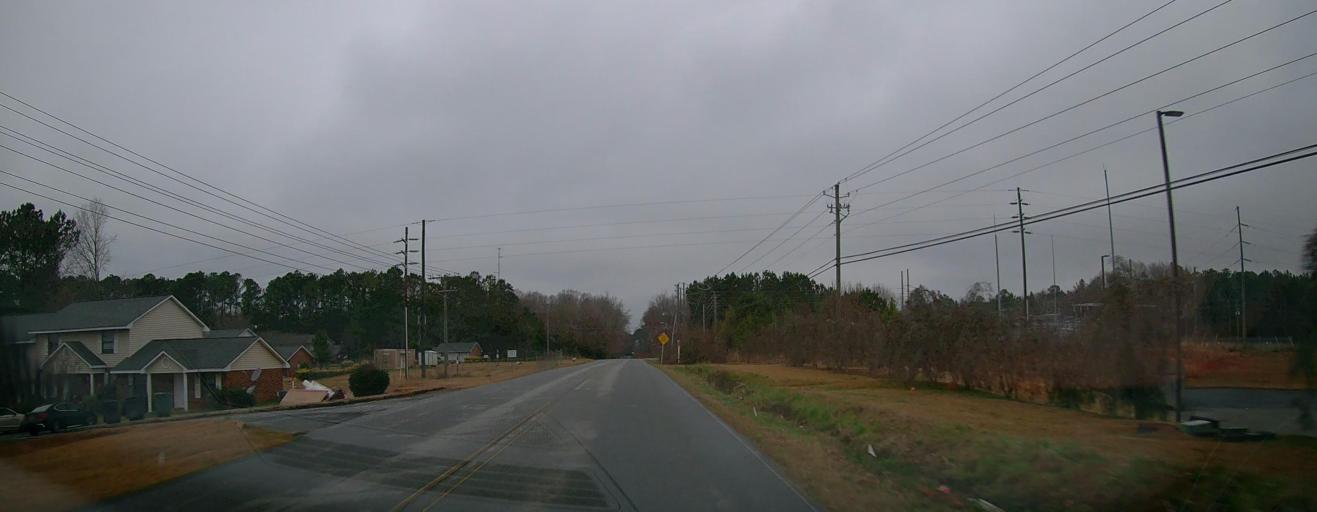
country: US
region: Georgia
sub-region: Pike County
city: Zebulon
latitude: 33.1133
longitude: -84.3429
